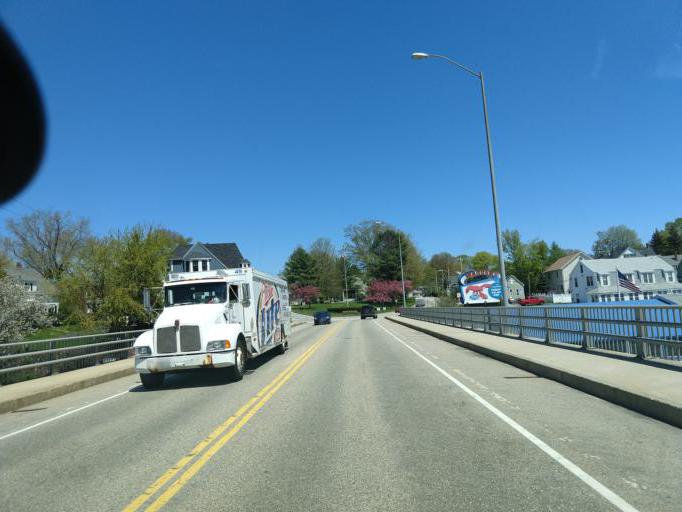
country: US
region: Maine
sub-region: York County
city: Kittery
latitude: 43.0835
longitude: -70.7510
